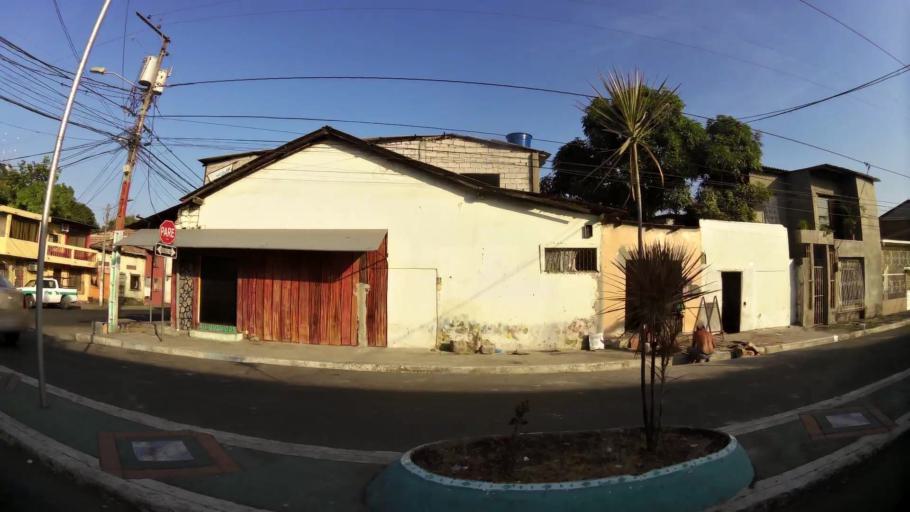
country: EC
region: Guayas
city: Eloy Alfaro
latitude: -2.1699
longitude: -79.8482
